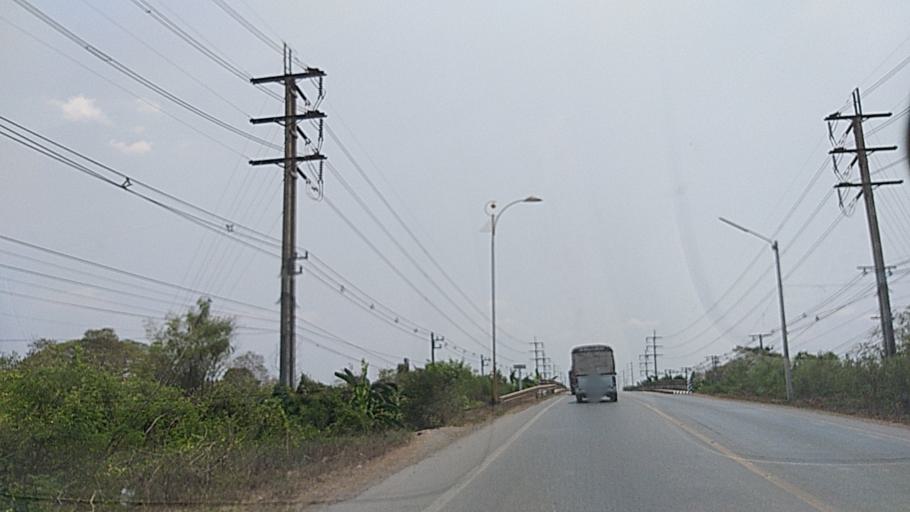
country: TH
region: Chachoengsao
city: Bang Nam Priao
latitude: 13.8448
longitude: 101.0517
